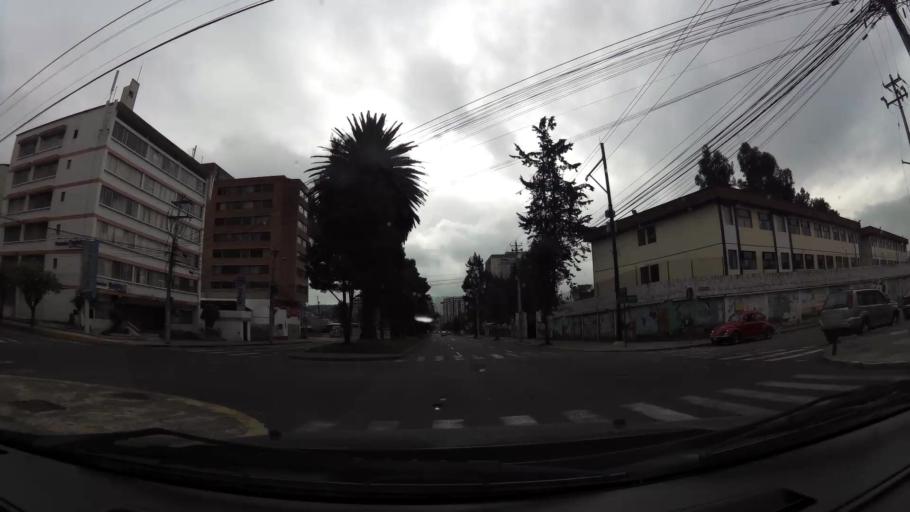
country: EC
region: Pichincha
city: Quito
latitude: -0.1935
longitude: -78.4910
